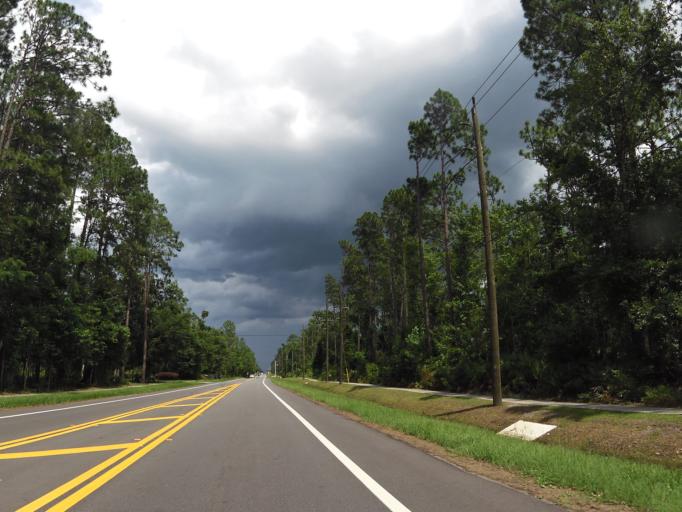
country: US
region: Florida
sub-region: Saint Johns County
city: Fruit Cove
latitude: 30.0636
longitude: -81.6572
